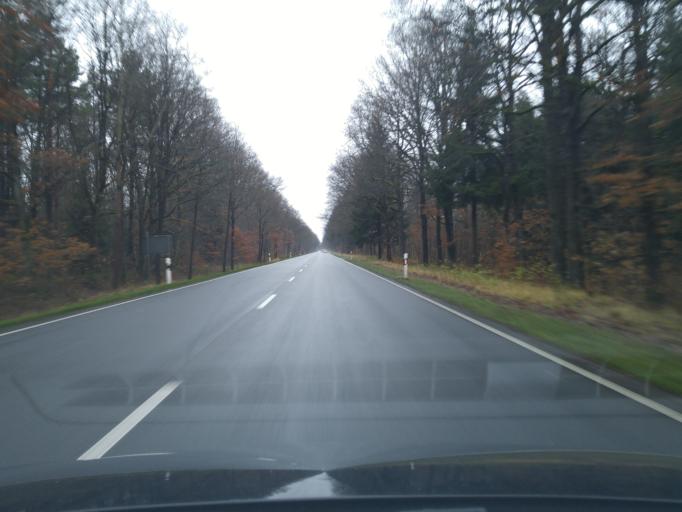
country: DE
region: Lower Saxony
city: Sprakensehl
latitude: 52.8151
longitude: 10.4878
